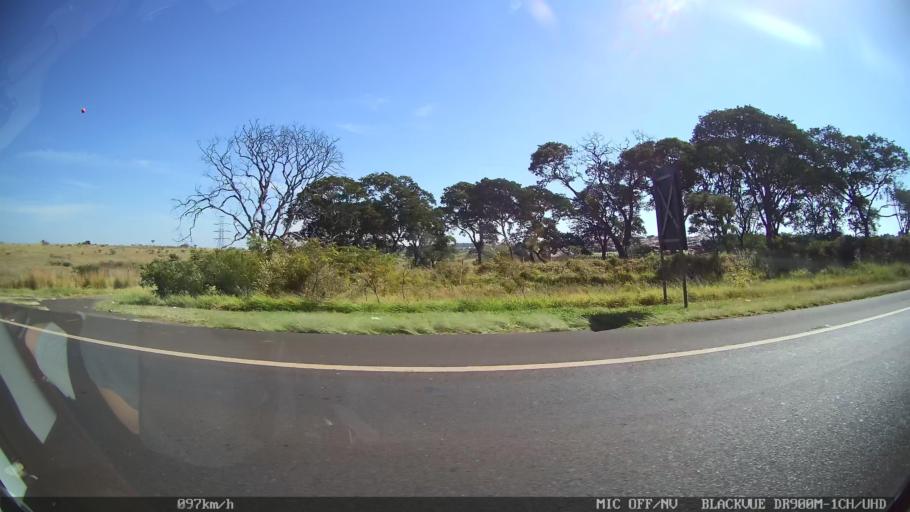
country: BR
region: Sao Paulo
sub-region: Franca
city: Franca
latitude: -20.5191
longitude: -47.4176
